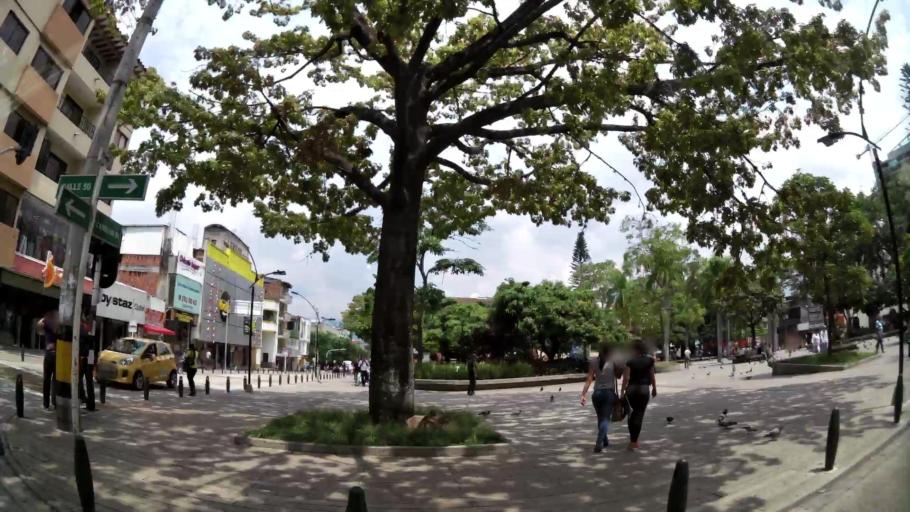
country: CO
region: Antioquia
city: Itagui
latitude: 6.1725
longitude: -75.6100
